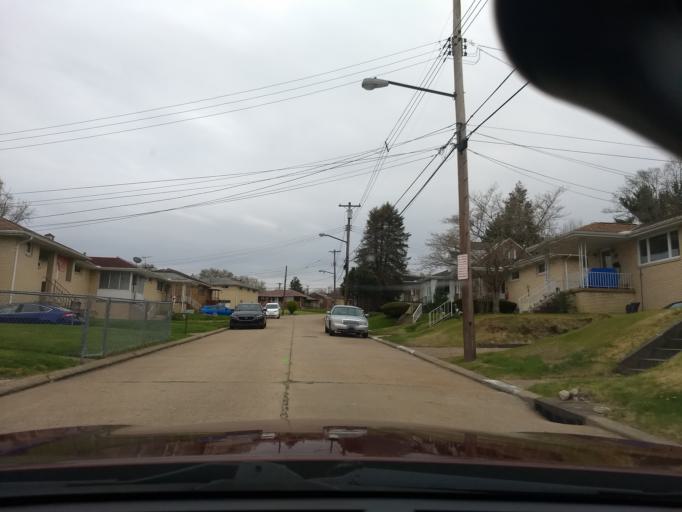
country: US
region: Pennsylvania
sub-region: Allegheny County
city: McKees Rocks
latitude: 40.4614
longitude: -80.0787
